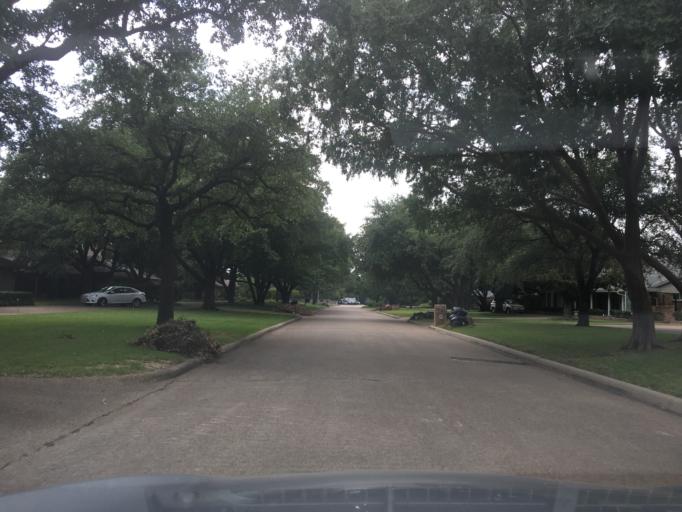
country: US
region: Texas
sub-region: Dallas County
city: University Park
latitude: 32.8961
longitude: -96.8175
